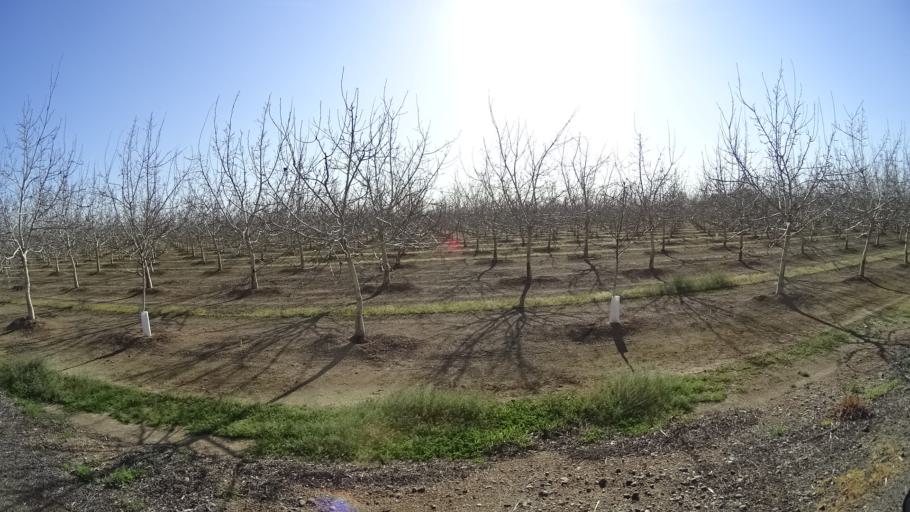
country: US
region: California
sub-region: Glenn County
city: Orland
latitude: 39.7593
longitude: -122.1134
